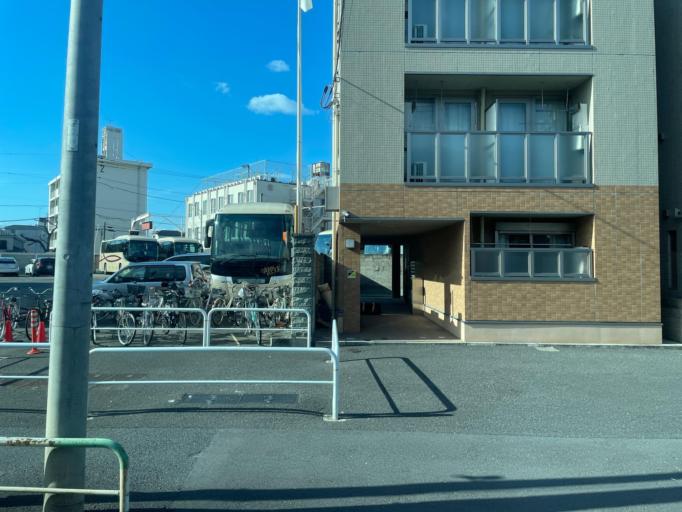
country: JP
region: Saitama
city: Kawaguchi
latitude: 35.7623
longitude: 139.7478
